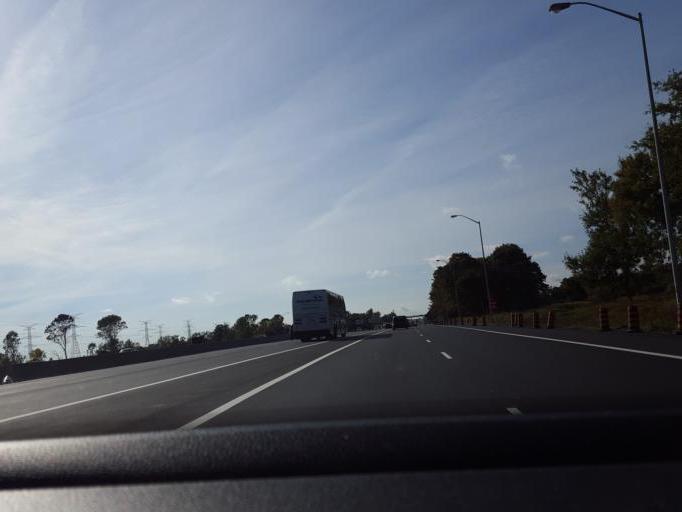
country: CA
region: Ontario
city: Oshawa
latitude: 43.9029
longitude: -78.6281
